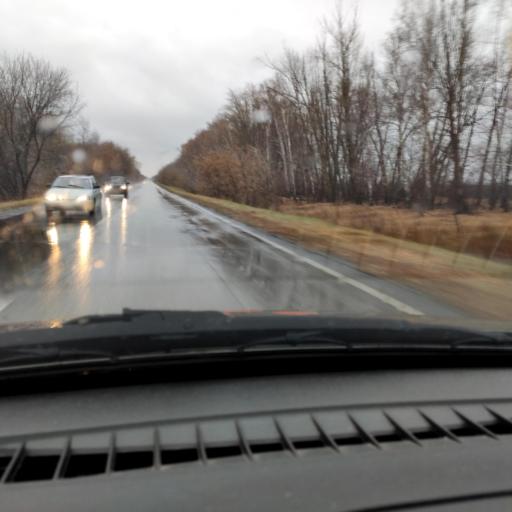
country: RU
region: Samara
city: Khryashchevka
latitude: 53.7295
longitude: 49.2053
